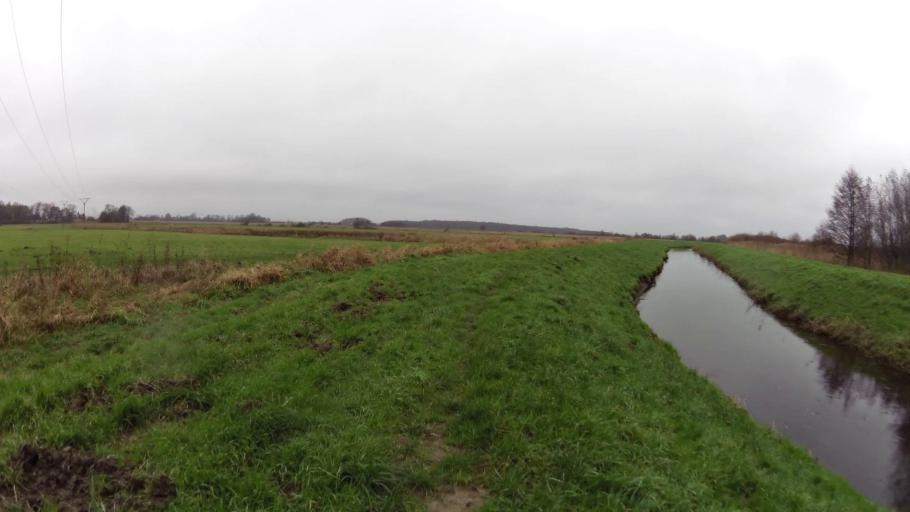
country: PL
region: West Pomeranian Voivodeship
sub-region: Koszalin
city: Koszalin
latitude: 54.2365
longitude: 16.1397
